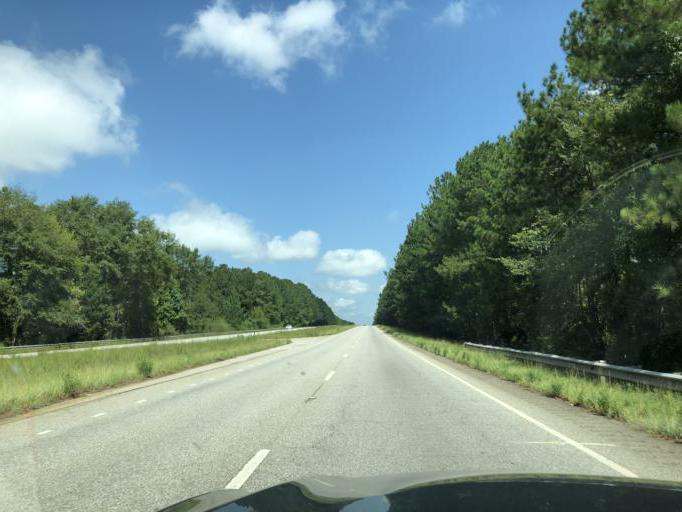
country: US
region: Alabama
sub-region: Henry County
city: Abbeville
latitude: 31.6430
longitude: -85.2807
